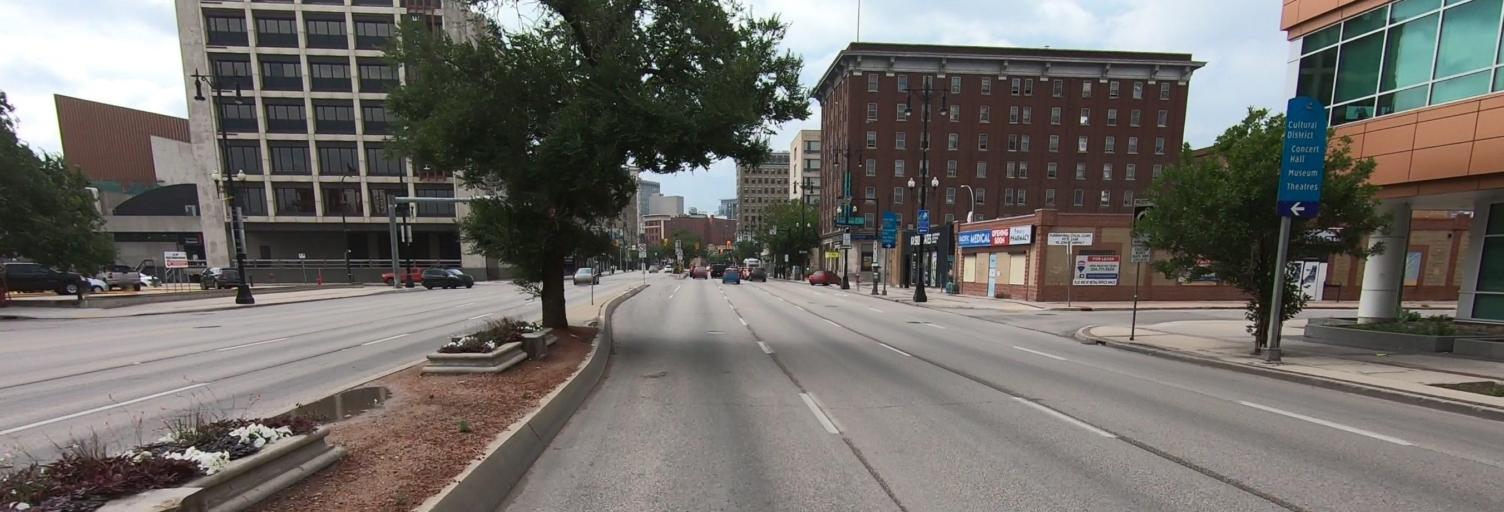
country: CA
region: Manitoba
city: Winnipeg
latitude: 49.9013
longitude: -97.1369
